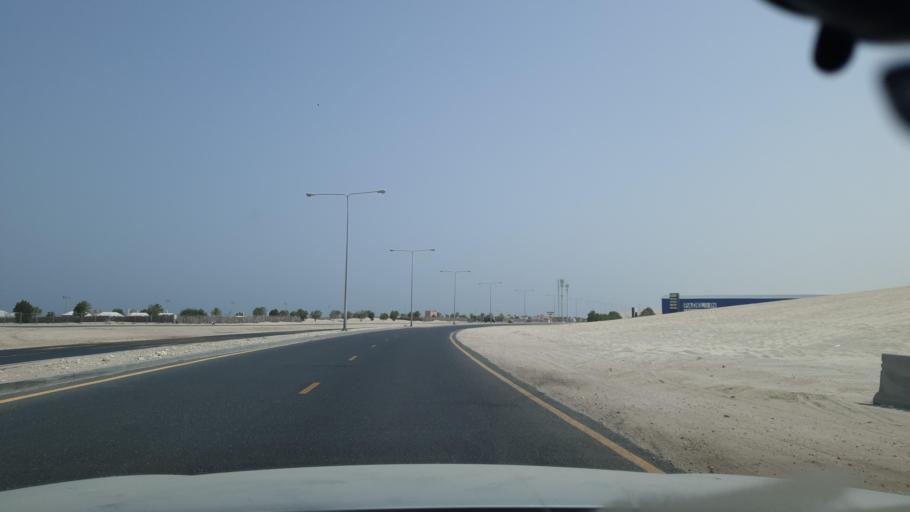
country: QA
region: Al Wakrah
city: Umm Sa'id
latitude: 24.8581
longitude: 51.5108
